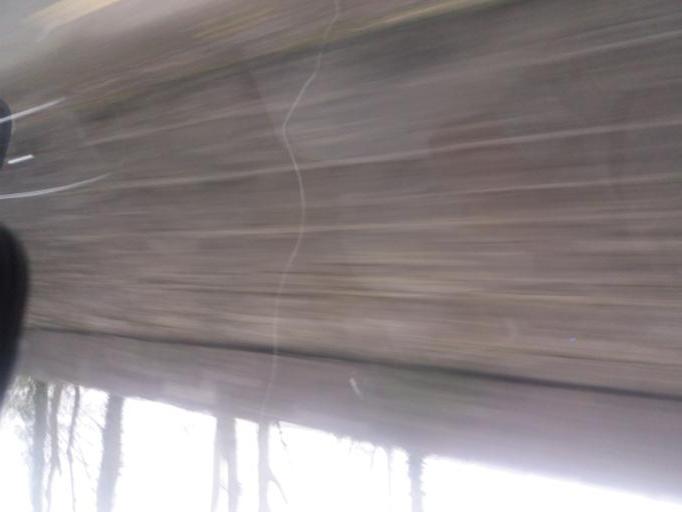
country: IE
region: Munster
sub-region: County Limerick
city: Adare
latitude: 52.5734
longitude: -8.7751
